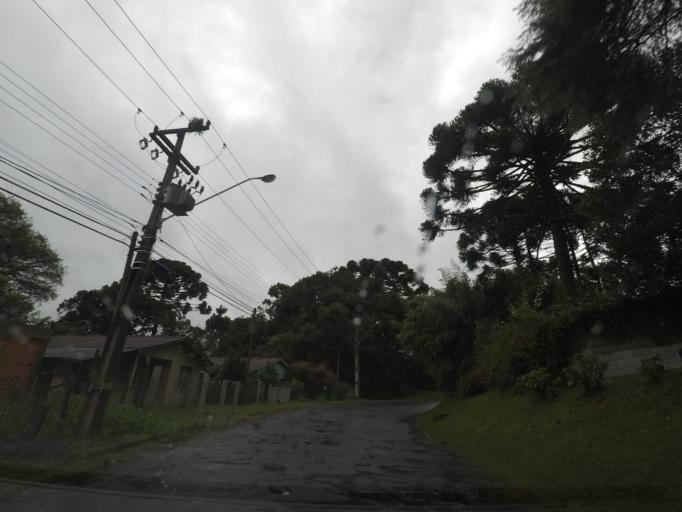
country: BR
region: Parana
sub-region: Campo Largo
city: Campo Largo
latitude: -25.4519
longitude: -49.4504
